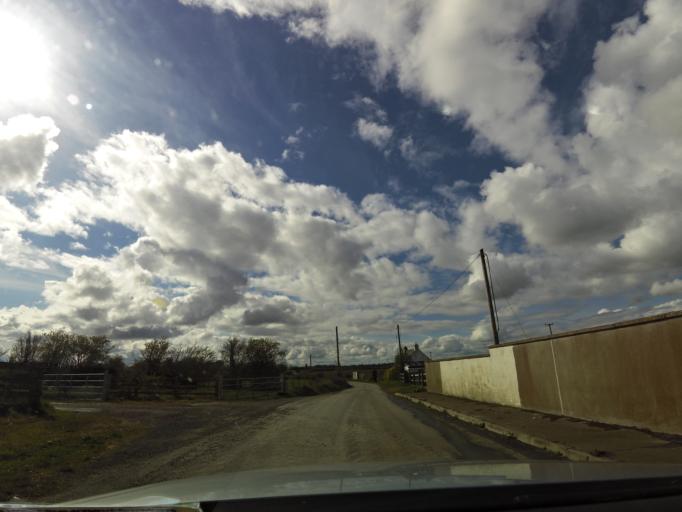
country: IE
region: Leinster
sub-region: Laois
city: Rathdowney
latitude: 52.7775
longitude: -7.5377
